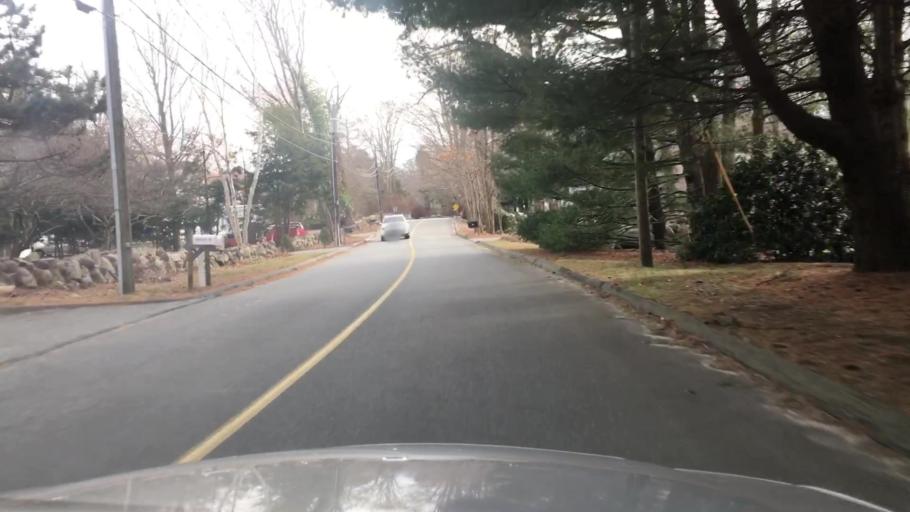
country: US
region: Connecticut
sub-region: Middlesex County
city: Essex Village
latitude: 41.3661
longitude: -72.4009
